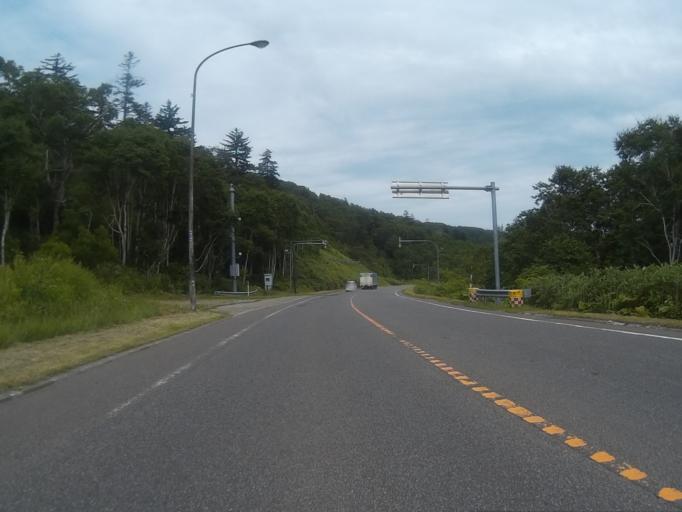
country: JP
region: Hokkaido
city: Sapporo
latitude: 42.8702
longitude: 141.1129
